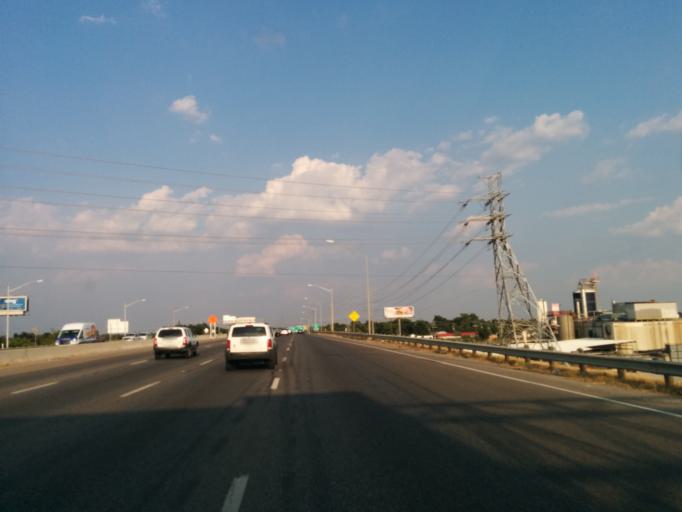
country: US
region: Texas
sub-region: Bexar County
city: San Antonio
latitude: 29.3951
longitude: -98.4900
